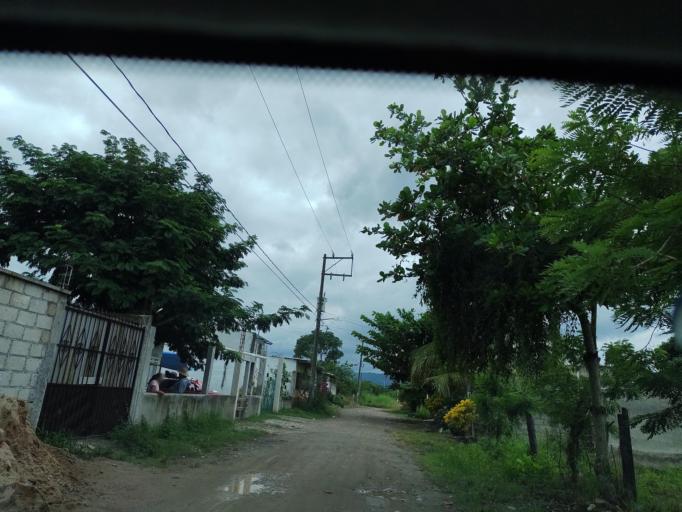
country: MX
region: Veracruz
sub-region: Atzalan
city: Colonias Pedernales
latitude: 20.0523
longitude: -97.0418
